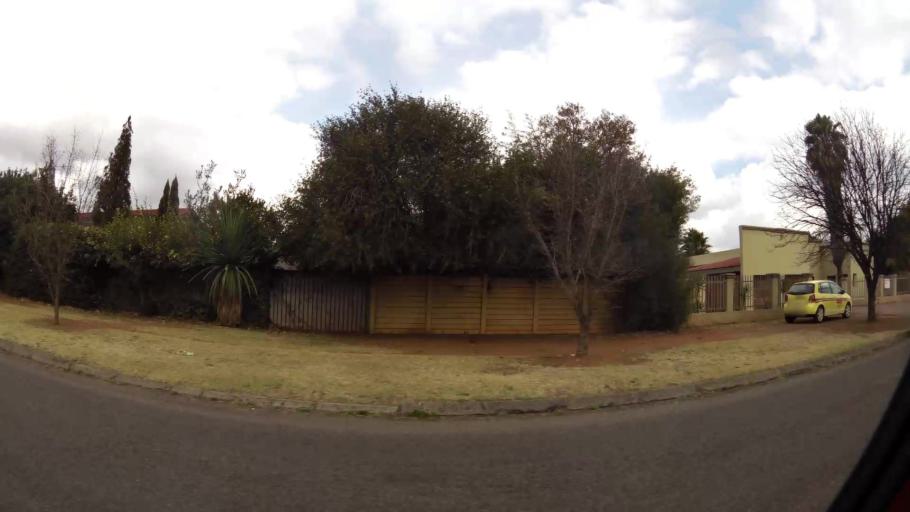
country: ZA
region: Gauteng
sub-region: Sedibeng District Municipality
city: Vanderbijlpark
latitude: -26.7315
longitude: 27.8492
